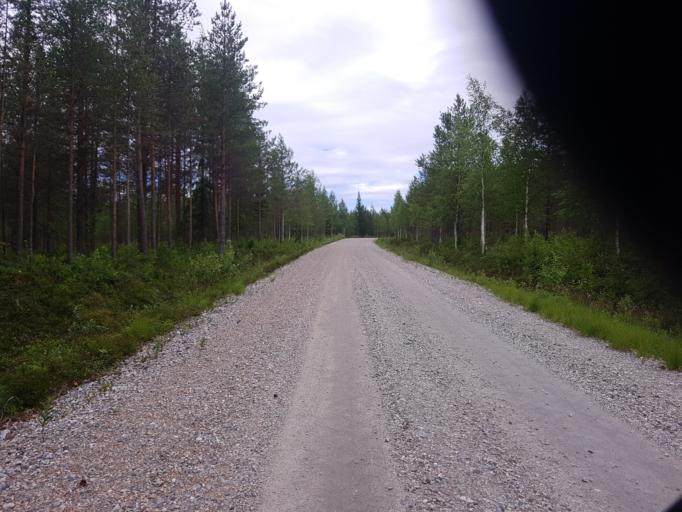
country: FI
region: Kainuu
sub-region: Kehys-Kainuu
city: Kuhmo
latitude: 64.4326
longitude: 29.5787
